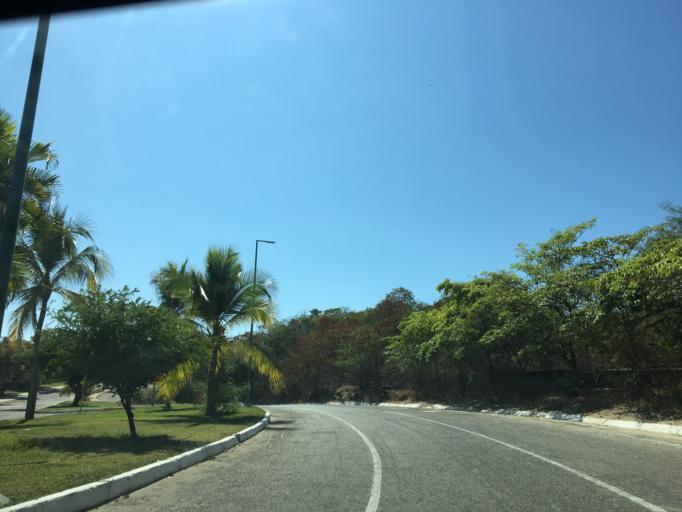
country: MX
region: Oaxaca
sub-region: Santa Maria Huatulco
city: Crucecita
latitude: 15.7858
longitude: -96.0604
